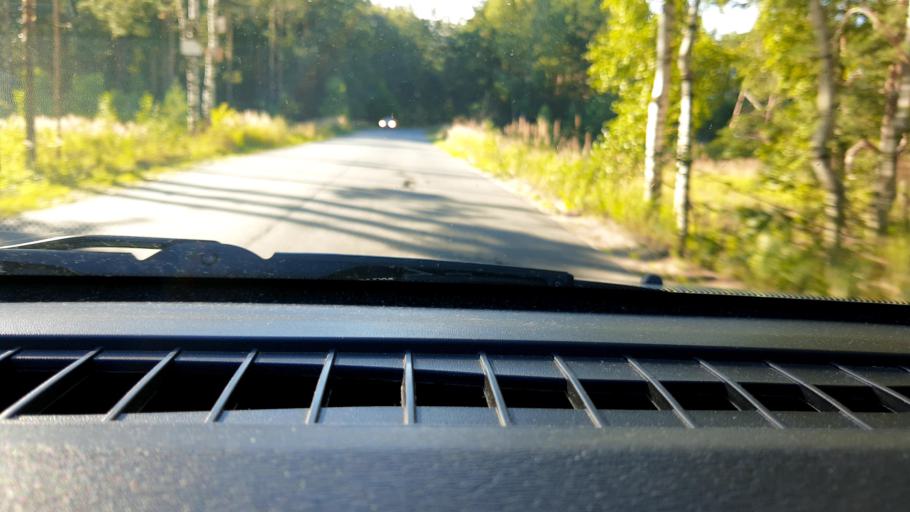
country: RU
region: Nizjnij Novgorod
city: Babino
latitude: 56.3310
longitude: 43.6216
